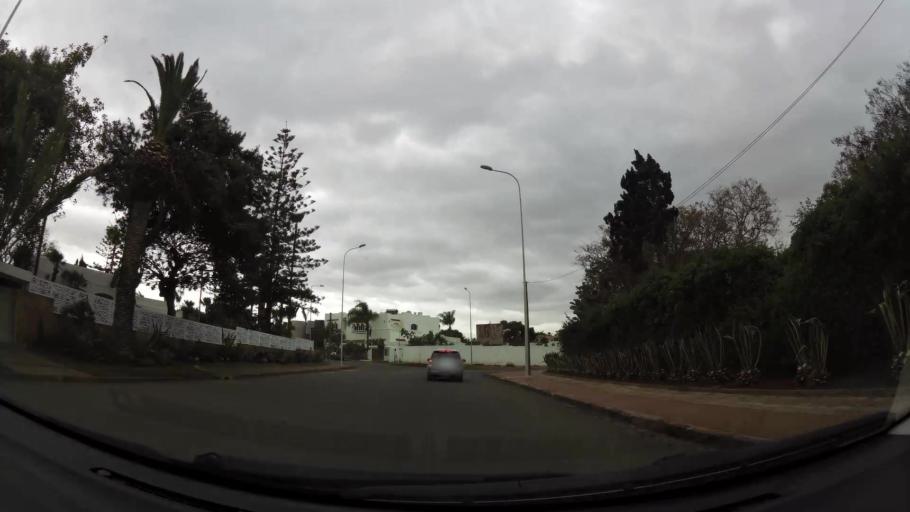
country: MA
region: Grand Casablanca
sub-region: Casablanca
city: Casablanca
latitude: 33.5828
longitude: -7.6696
